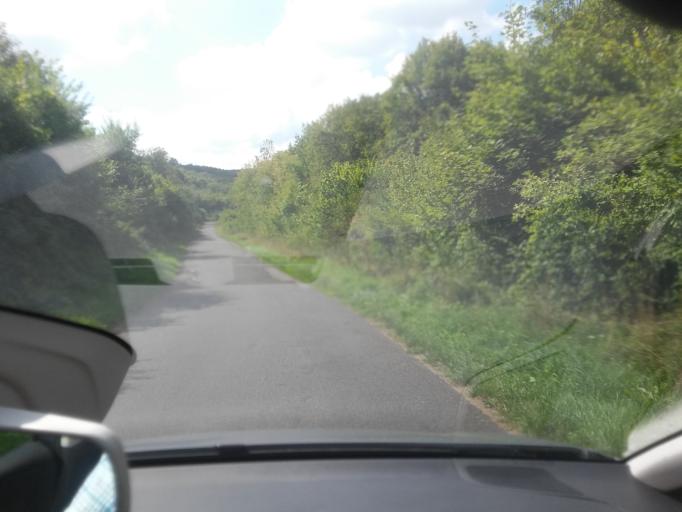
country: FR
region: Lorraine
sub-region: Departement de la Meuse
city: Montmedy
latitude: 49.4967
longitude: 5.4178
